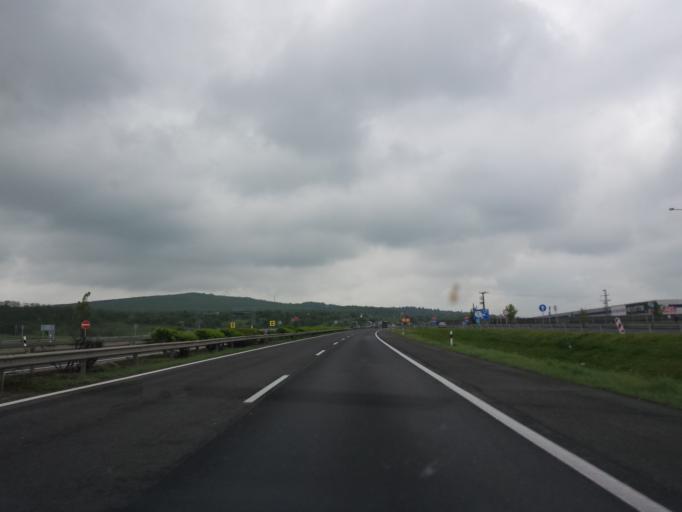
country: HU
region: Pest
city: Biatorbagy
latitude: 47.4947
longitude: 18.8186
